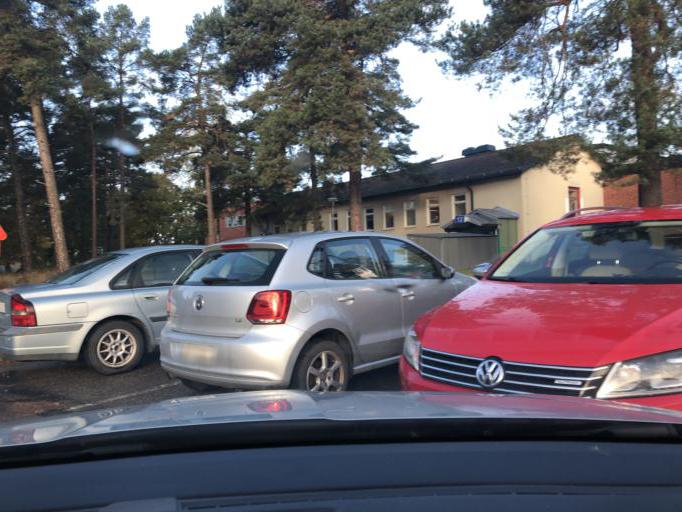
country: SE
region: Vaestmanland
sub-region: Vasteras
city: Vasteras
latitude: 59.6199
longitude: 16.5809
